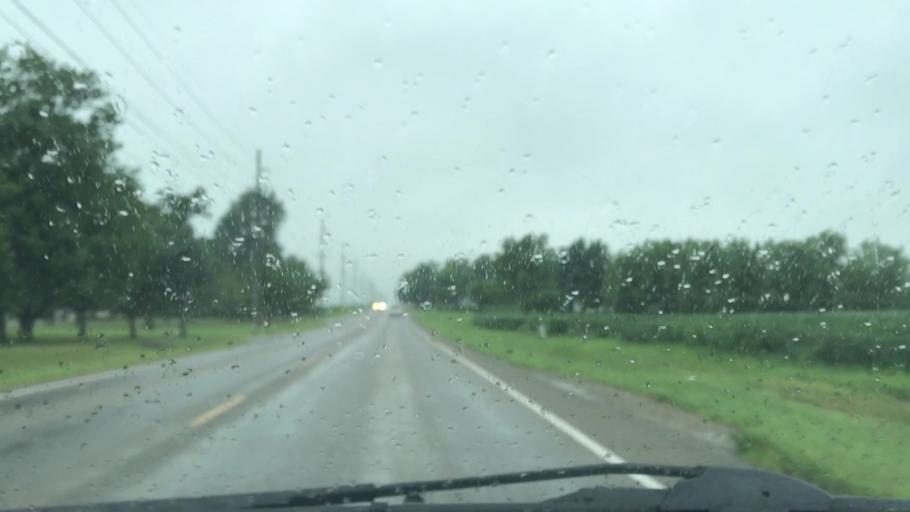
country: US
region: Indiana
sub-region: Hamilton County
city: Westfield
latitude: 40.1058
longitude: -86.1545
